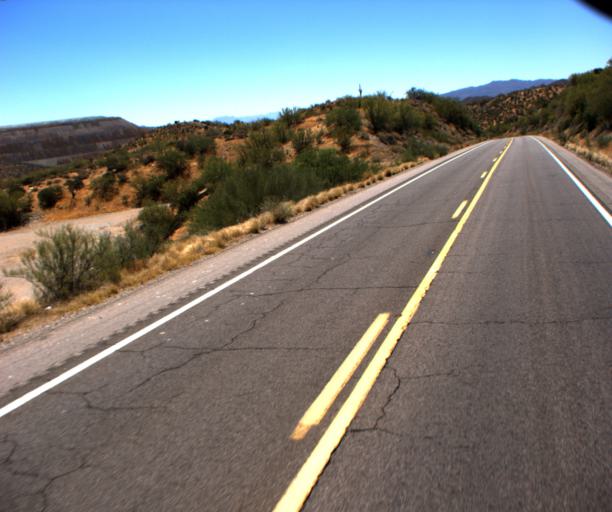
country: US
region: Arizona
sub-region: Pinal County
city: Kearny
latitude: 33.1341
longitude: -110.9880
